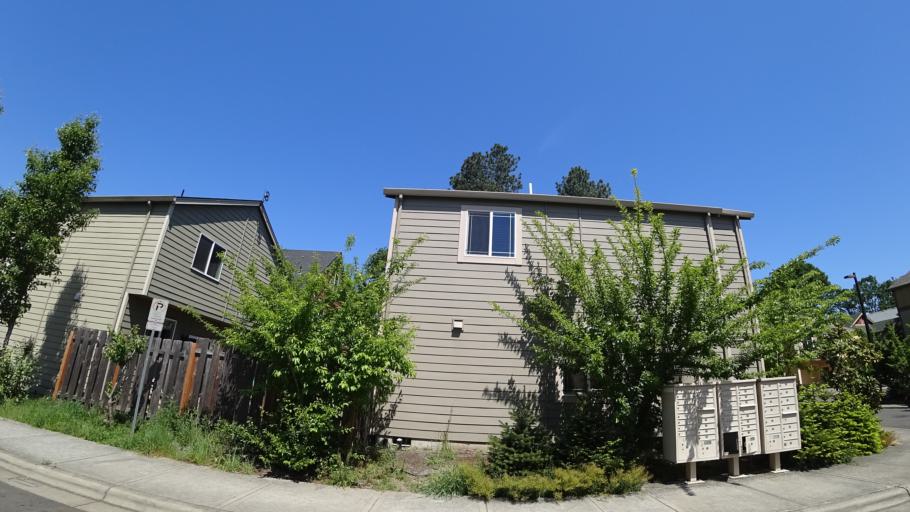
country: US
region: Oregon
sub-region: Washington County
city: Aloha
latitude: 45.4973
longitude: -122.8557
